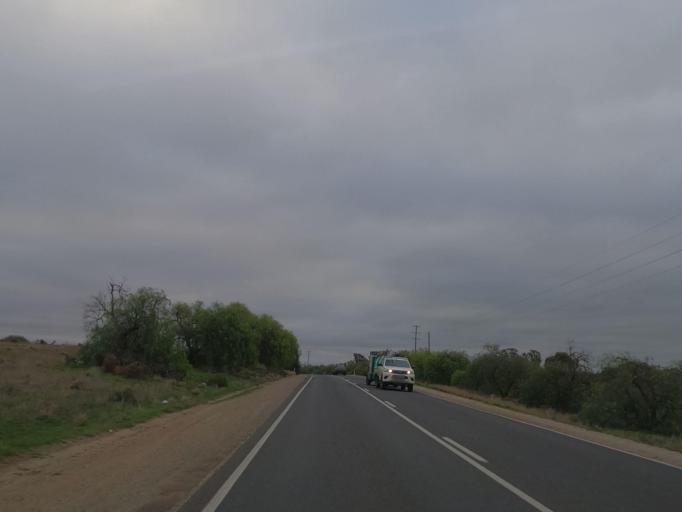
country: AU
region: Victoria
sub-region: Swan Hill
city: Swan Hill
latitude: -35.4467
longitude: 143.6208
